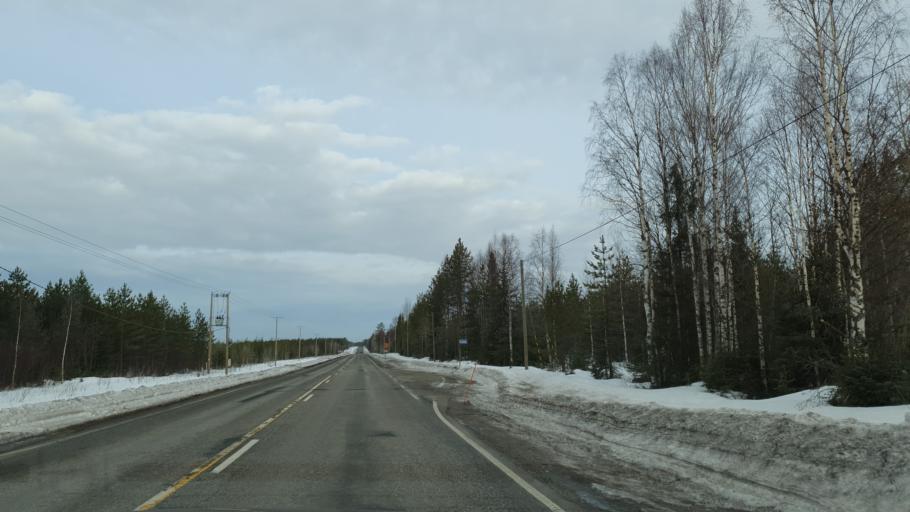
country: FI
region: Kainuu
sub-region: Kajaani
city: Vuokatti
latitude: 64.2038
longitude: 28.1558
